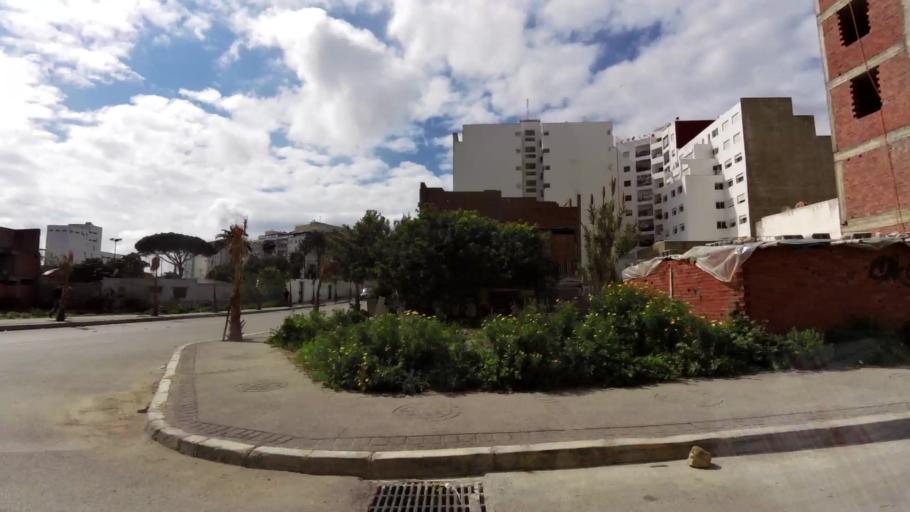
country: MA
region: Tanger-Tetouan
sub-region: Tanger-Assilah
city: Tangier
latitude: 35.7684
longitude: -5.8102
